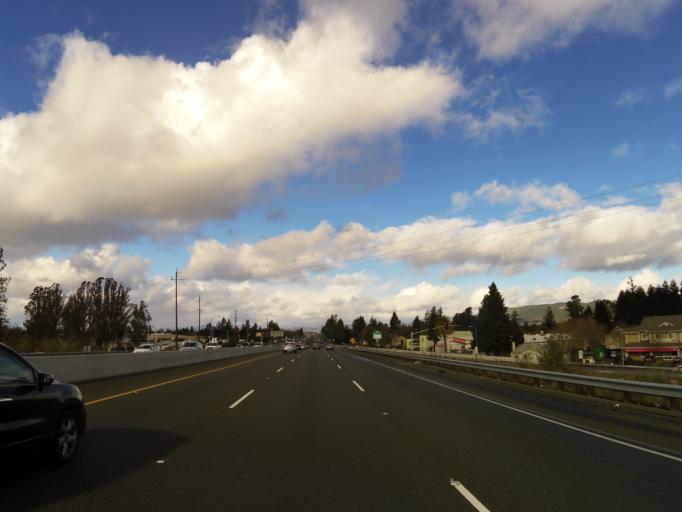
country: US
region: California
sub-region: Sonoma County
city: Cotati
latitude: 38.3319
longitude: -122.7127
